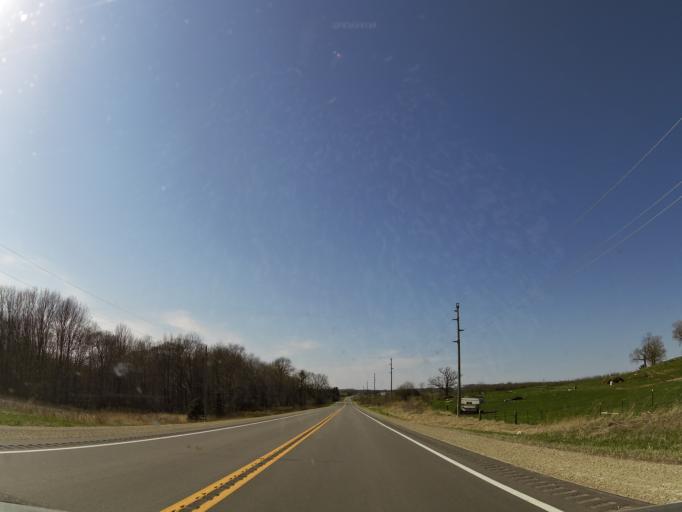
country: US
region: Wisconsin
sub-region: Pierce County
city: Ellsworth
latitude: 44.7085
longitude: -92.4200
